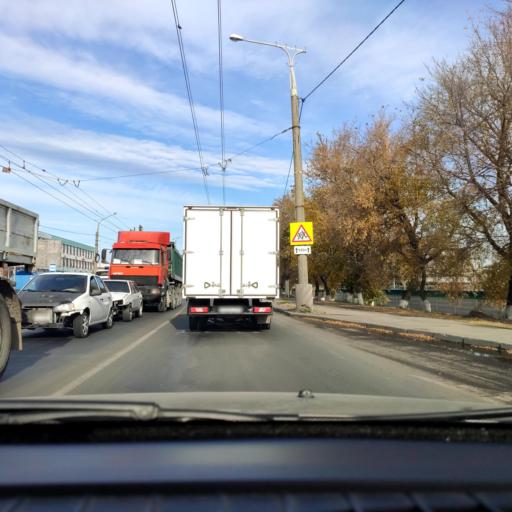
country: RU
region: Samara
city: Tol'yatti
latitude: 53.5356
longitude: 49.4407
